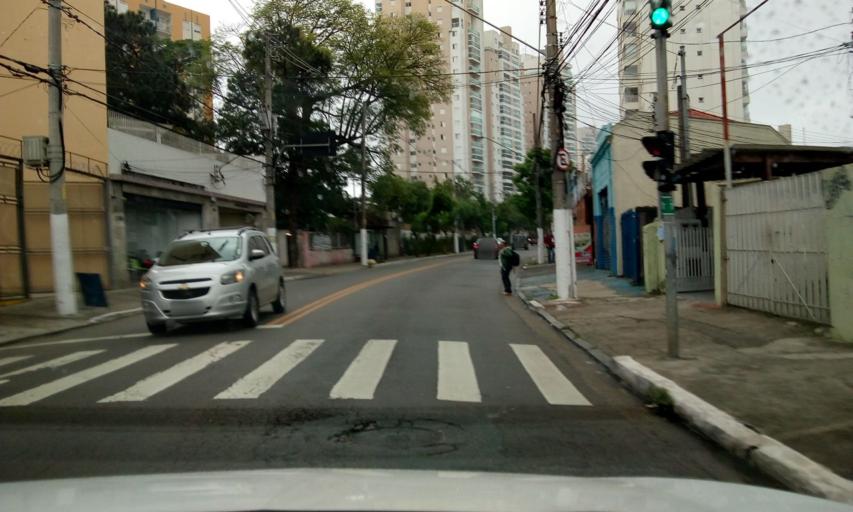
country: BR
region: Sao Paulo
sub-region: Sao Paulo
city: Sao Paulo
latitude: -23.5864
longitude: -46.6282
